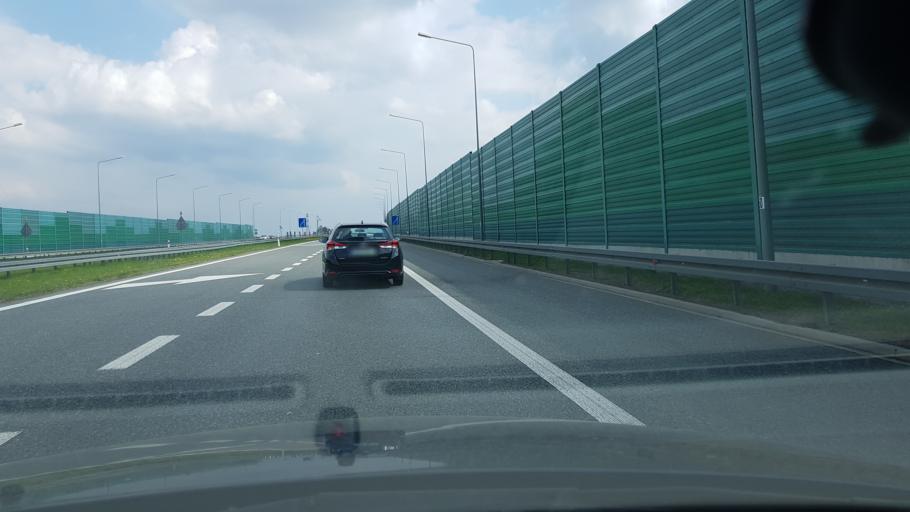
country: PL
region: Masovian Voivodeship
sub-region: Powiat minski
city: Kaluszyn
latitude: 52.1999
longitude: 21.7664
